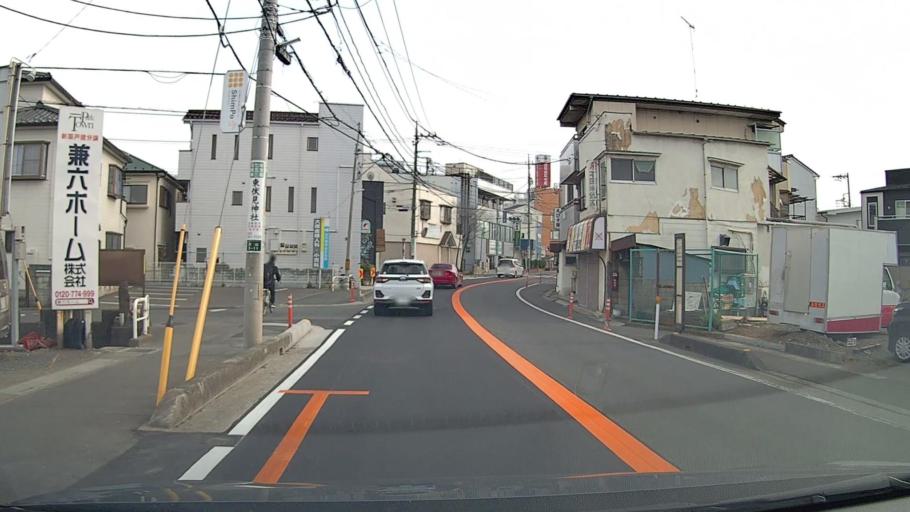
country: JP
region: Tokyo
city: Tanashicho
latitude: 35.7693
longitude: 139.5652
